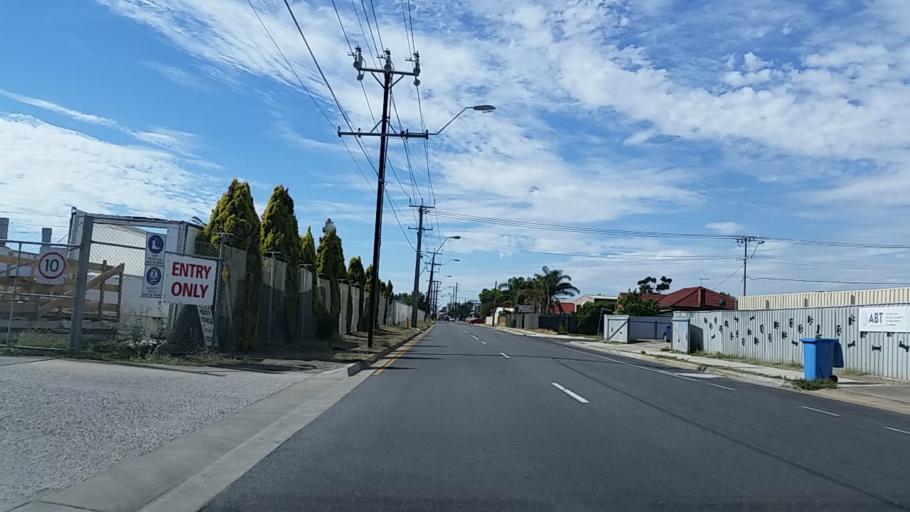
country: AU
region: South Australia
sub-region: Charles Sturt
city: Woodville North
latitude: -34.8564
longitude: 138.5383
